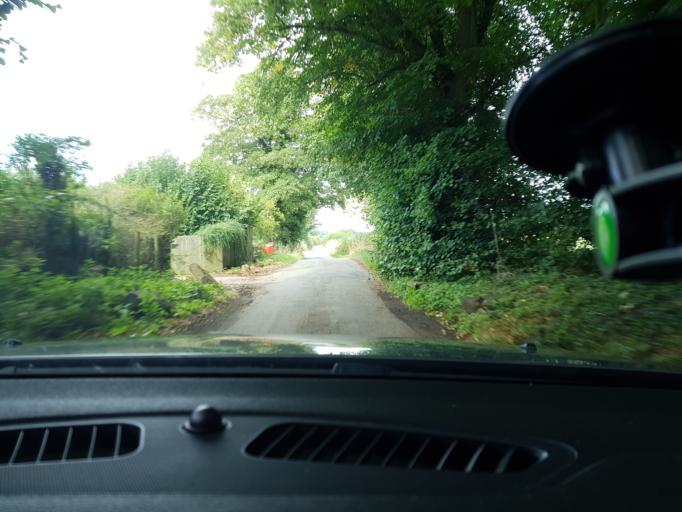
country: GB
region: England
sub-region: West Berkshire
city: Hungerford
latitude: 51.3954
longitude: -1.4888
